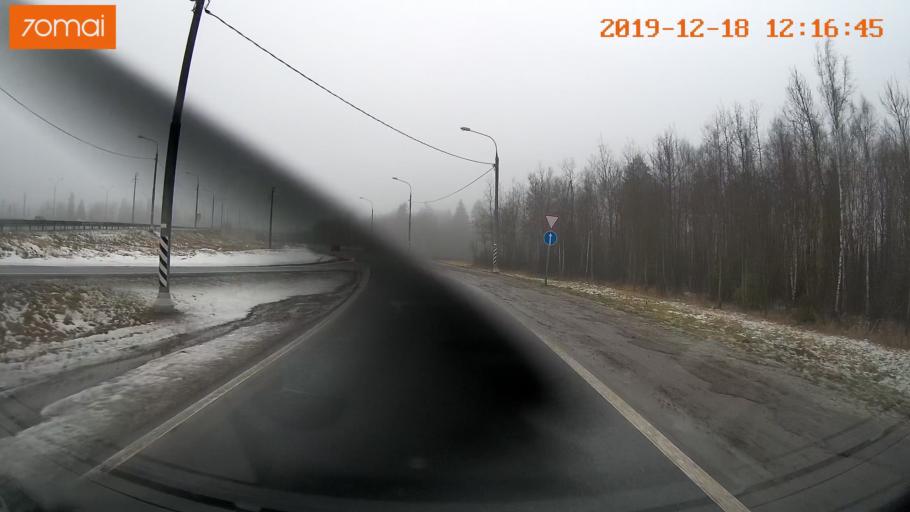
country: RU
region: Moskovskaya
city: Novopetrovskoye
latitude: 55.9803
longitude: 36.4614
